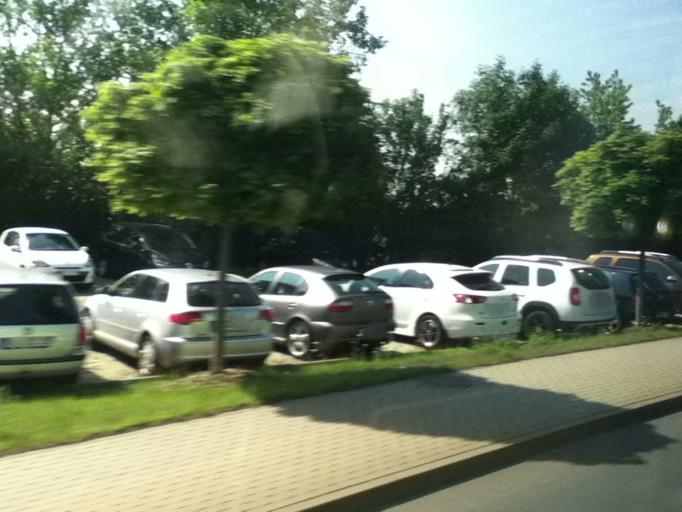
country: DE
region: Thuringia
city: Gera
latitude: 50.8915
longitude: 12.0779
